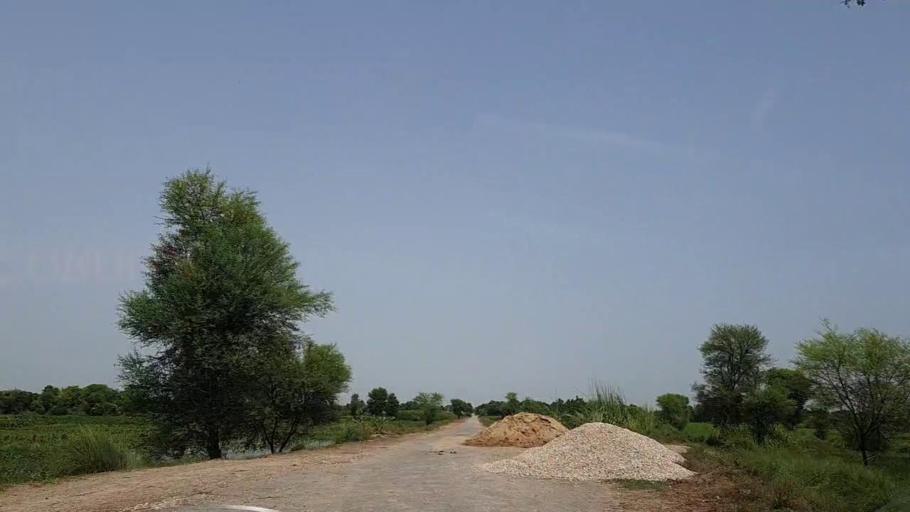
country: PK
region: Sindh
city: Tharu Shah
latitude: 26.9438
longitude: 68.0250
